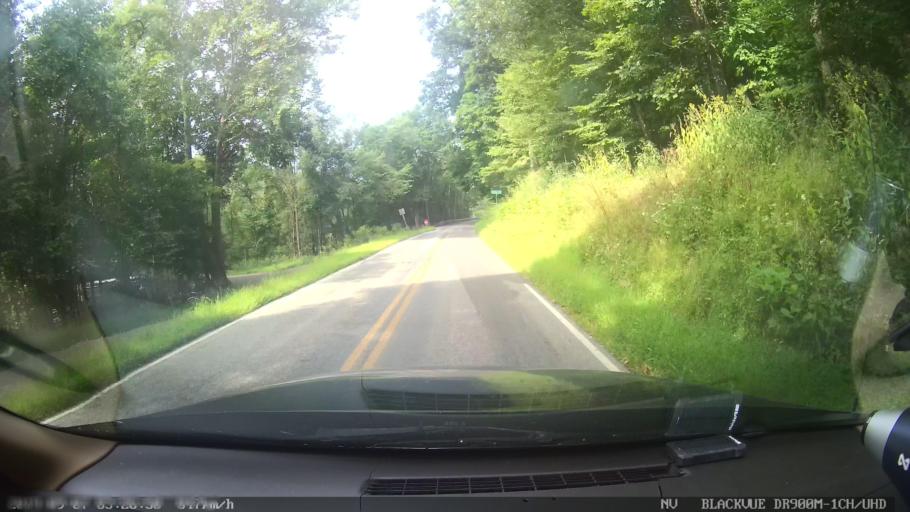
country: US
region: Ohio
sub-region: Licking County
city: Granville
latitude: 40.1234
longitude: -82.4972
